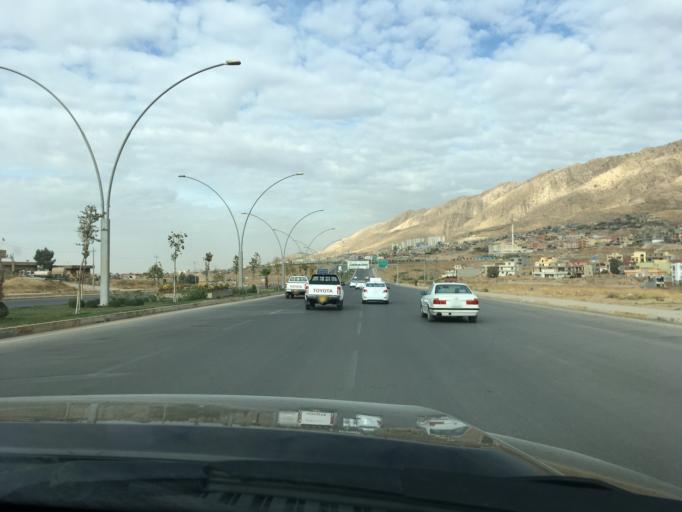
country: IQ
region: Dahuk
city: Sinah
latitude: 36.8470
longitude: 43.0587
